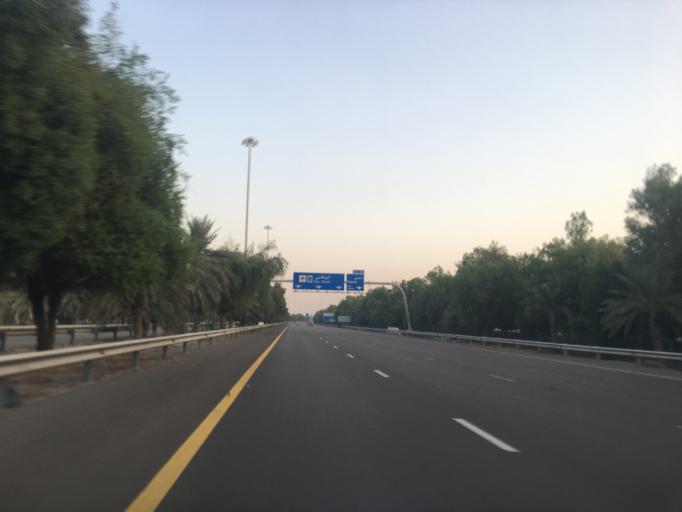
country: AE
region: Abu Dhabi
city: Abu Dhabi
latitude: 24.3429
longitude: 54.5751
